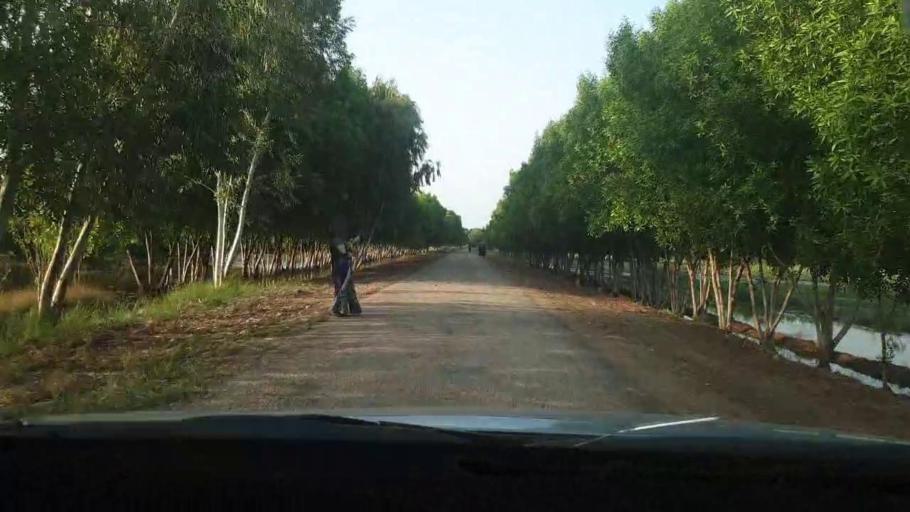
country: PK
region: Sindh
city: Pithoro
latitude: 25.6124
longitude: 69.4423
